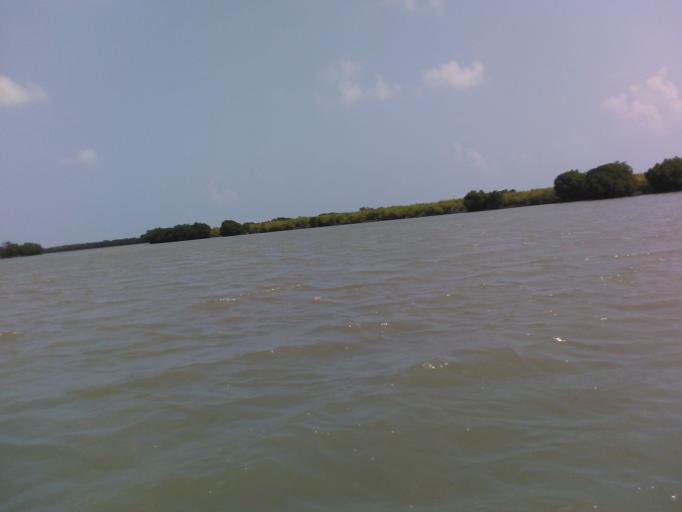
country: IN
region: Tamil Nadu
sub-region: Cuddalore
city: Annamalainagar
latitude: 11.4379
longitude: 79.7843
